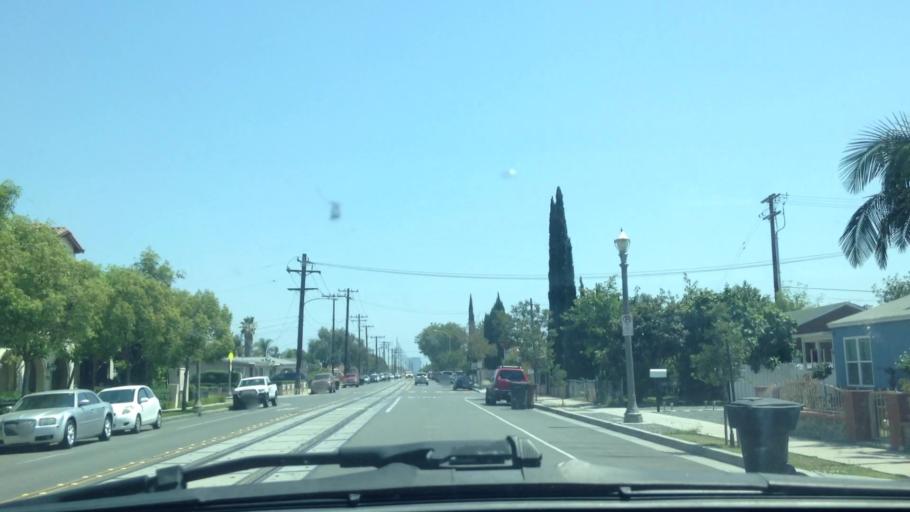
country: US
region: California
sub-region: Orange County
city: Anaheim
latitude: 33.8283
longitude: -117.9075
